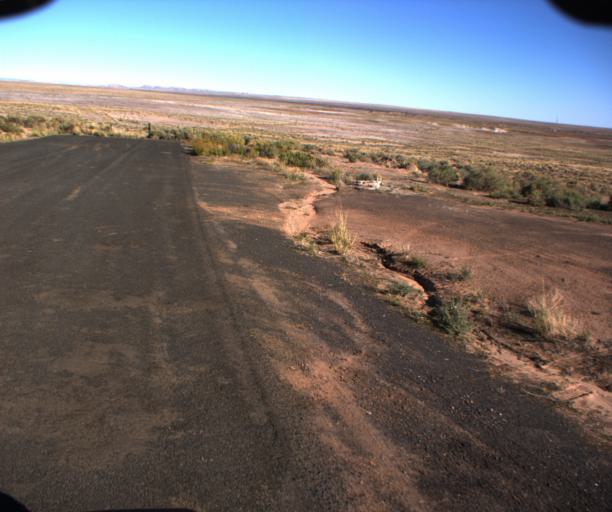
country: US
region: Arizona
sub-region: Navajo County
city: Holbrook
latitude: 34.9400
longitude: -110.1267
